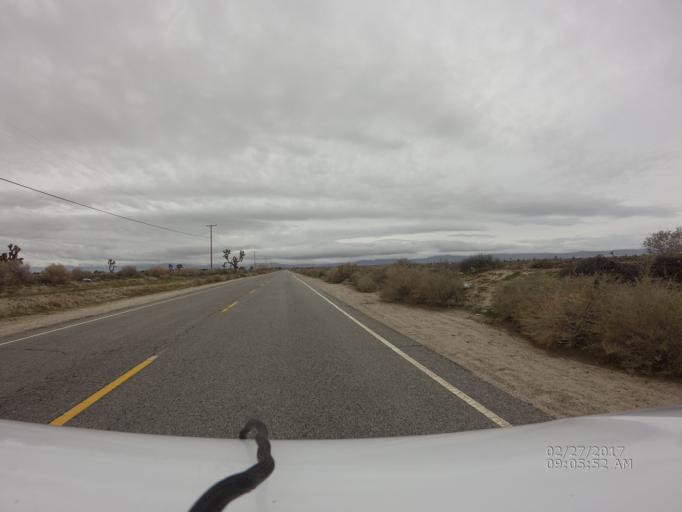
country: US
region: California
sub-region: Los Angeles County
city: Lancaster
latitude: 34.7278
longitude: -118.0770
